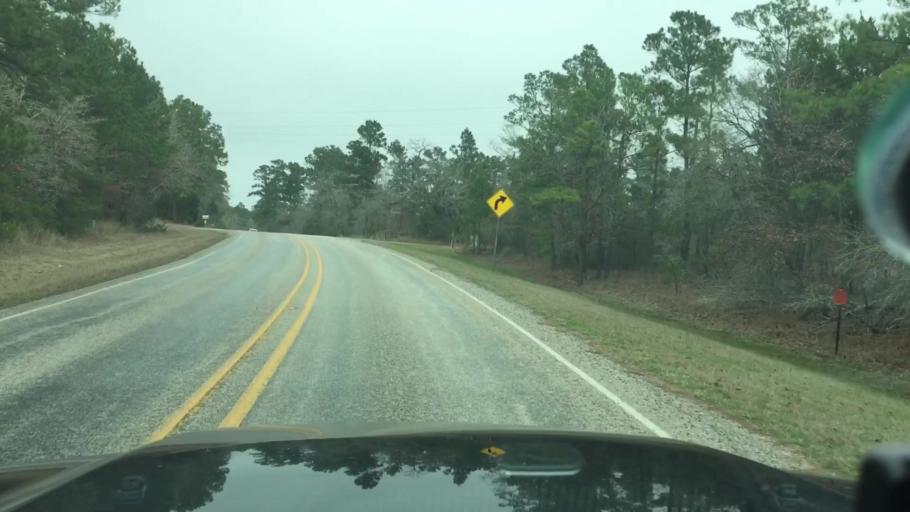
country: US
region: Texas
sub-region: Fayette County
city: La Grange
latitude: 30.0061
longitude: -96.9449
